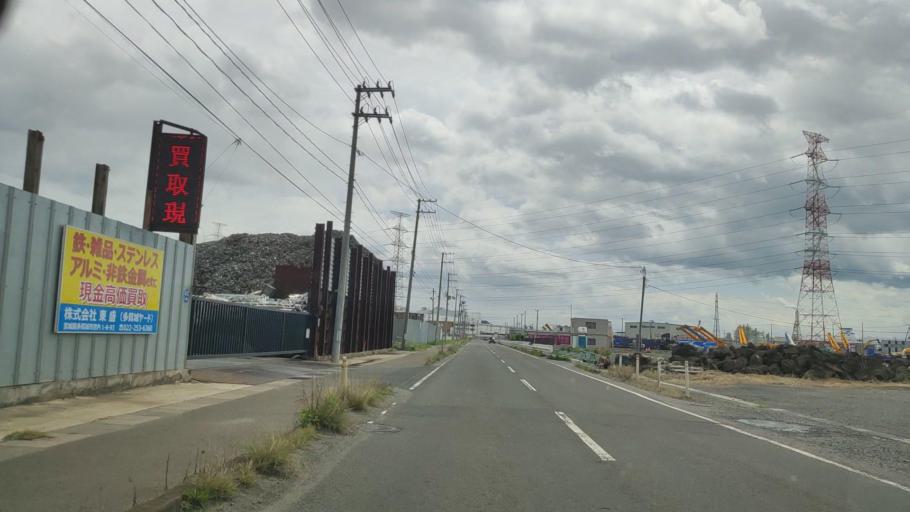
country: JP
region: Miyagi
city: Shiogama
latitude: 38.2811
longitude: 141.0080
